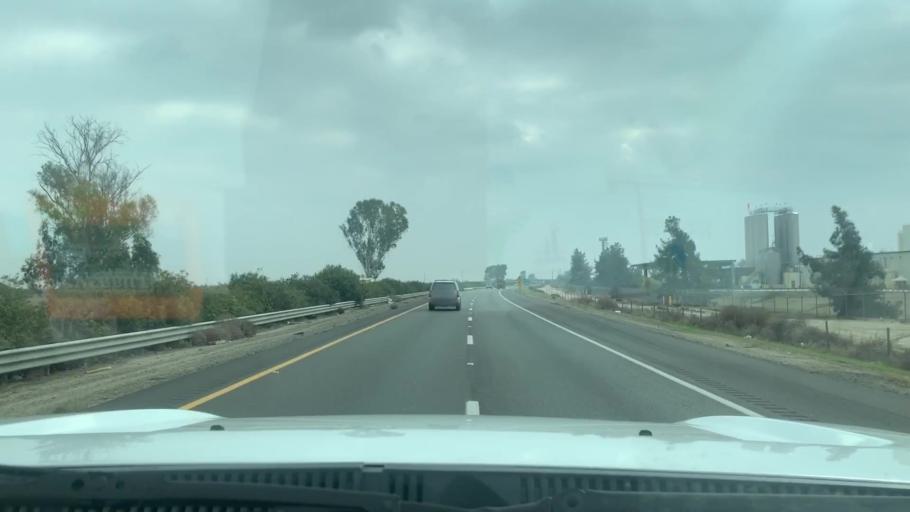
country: US
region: California
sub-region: Tulare County
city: Tipton
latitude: 36.1338
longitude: -119.3260
